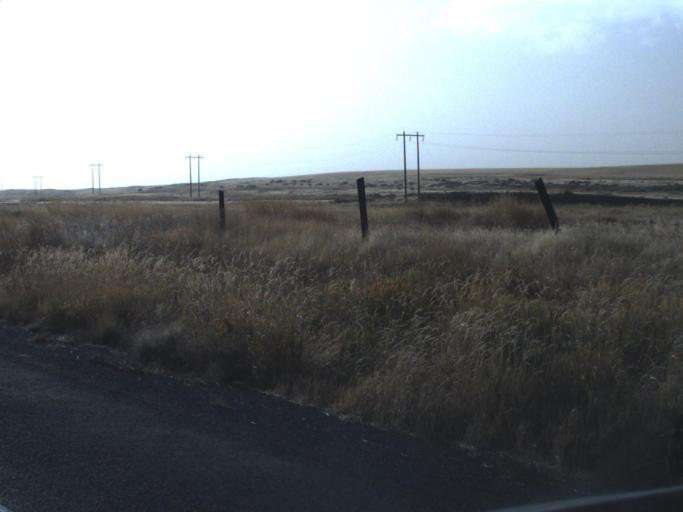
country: US
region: Washington
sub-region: Lincoln County
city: Davenport
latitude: 47.5246
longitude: -118.2078
